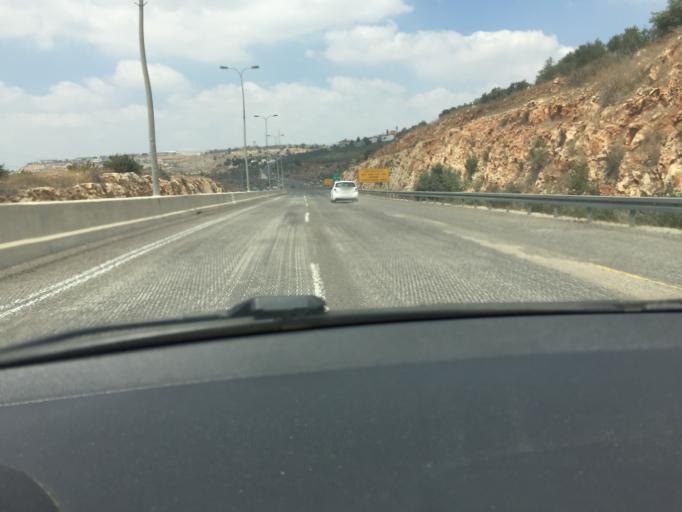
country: PS
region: West Bank
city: Haris
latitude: 32.1096
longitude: 35.1454
